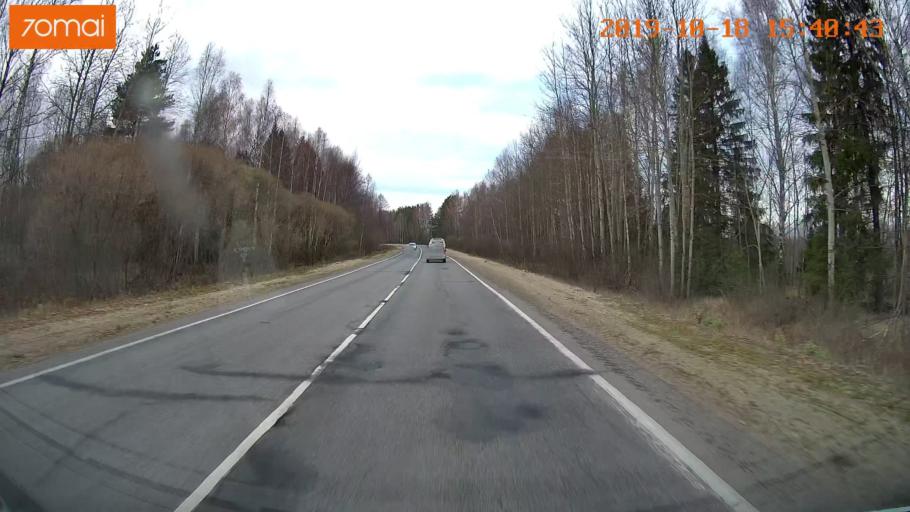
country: RU
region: Vladimir
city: Golovino
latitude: 55.9377
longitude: 40.5921
